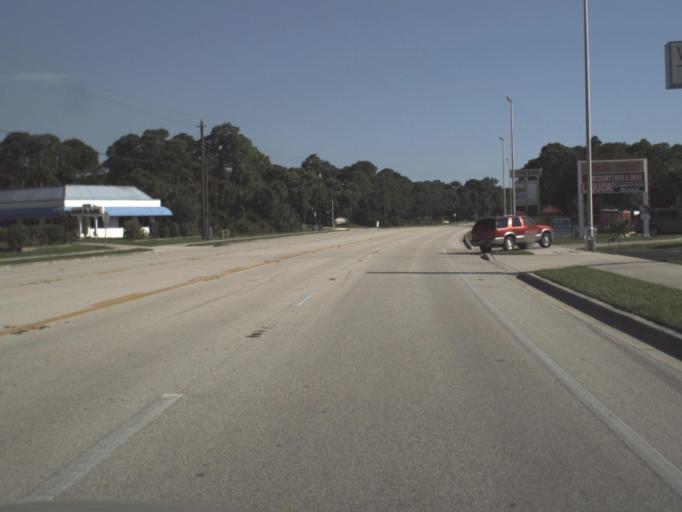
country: US
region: Florida
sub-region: Sarasota County
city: Englewood
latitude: 26.9746
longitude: -82.3545
